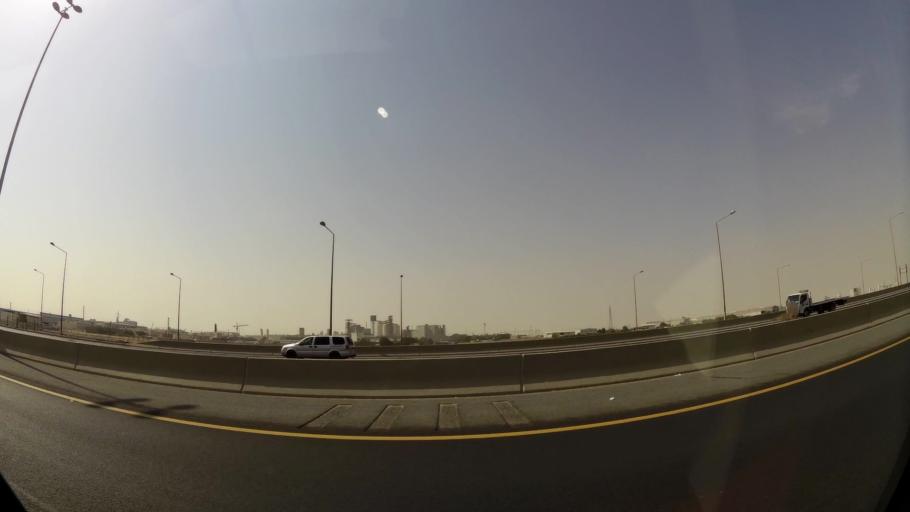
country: KW
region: Al Ahmadi
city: Al Fahahil
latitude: 29.0073
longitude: 48.1348
